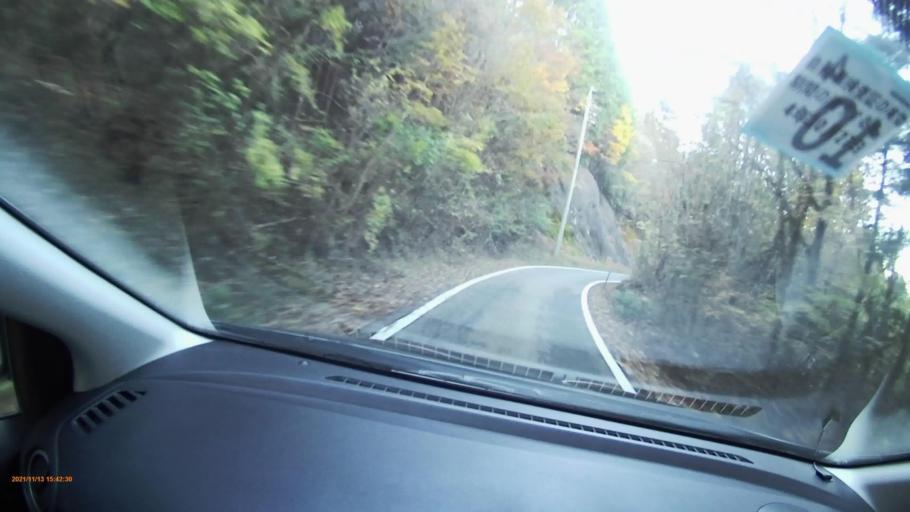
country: JP
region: Gifu
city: Nakatsugawa
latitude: 35.5925
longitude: 137.3922
